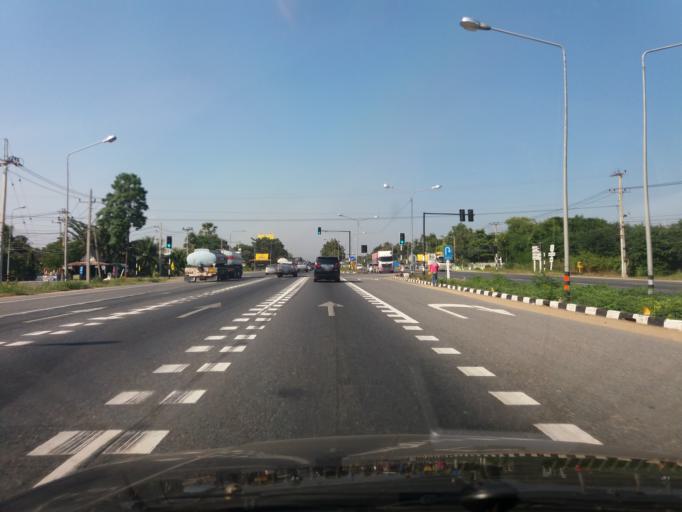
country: TH
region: Nakhon Sawan
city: Krok Phra
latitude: 15.5510
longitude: 100.1276
